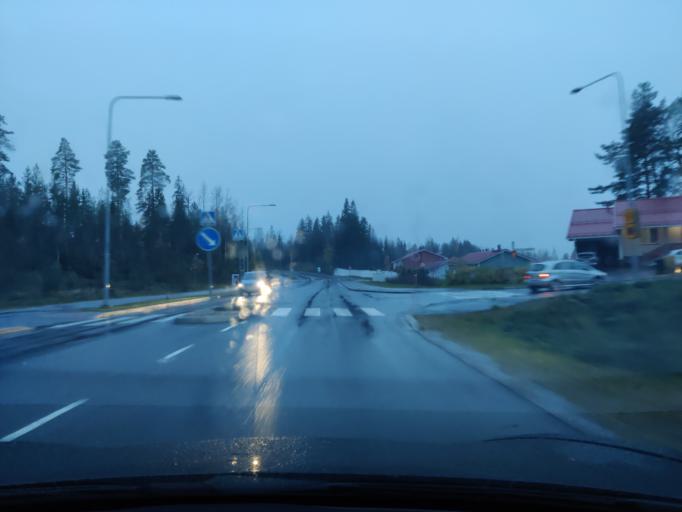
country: FI
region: Northern Savo
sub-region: Kuopio
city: Kuopio
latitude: 62.8306
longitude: 27.7058
